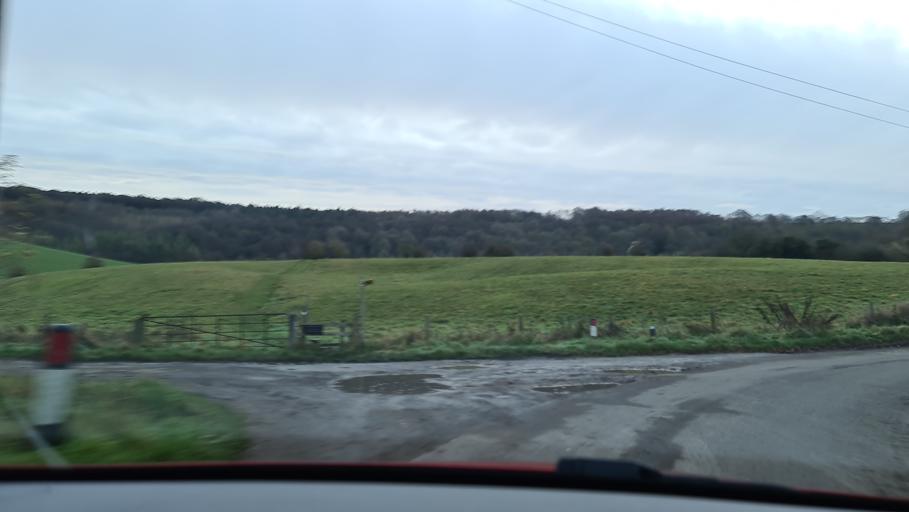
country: GB
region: England
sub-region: Buckinghamshire
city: Princes Risborough
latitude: 51.7161
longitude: -0.8141
